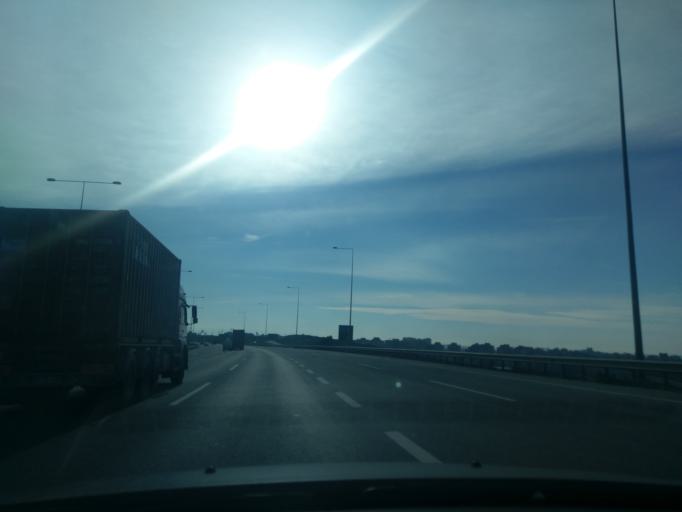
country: TR
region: Istanbul
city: Basaksehir
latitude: 41.1320
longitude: 28.8046
